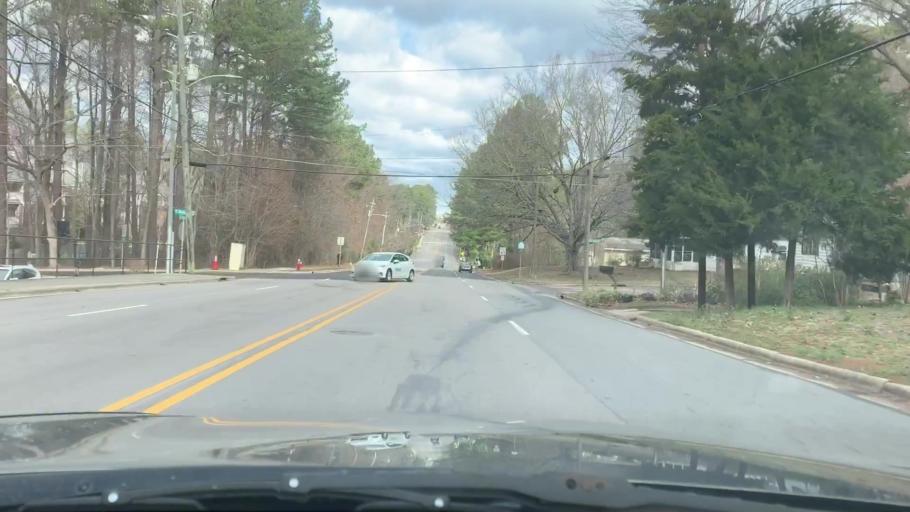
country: US
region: North Carolina
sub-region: Wake County
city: Cary
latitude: 35.7941
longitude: -78.7831
